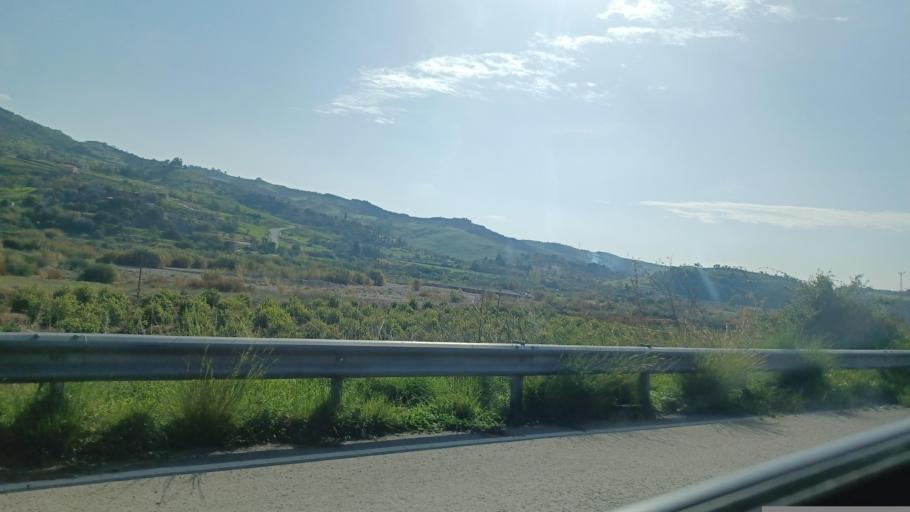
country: CY
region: Pafos
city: Mesogi
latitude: 34.7778
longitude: 32.5806
